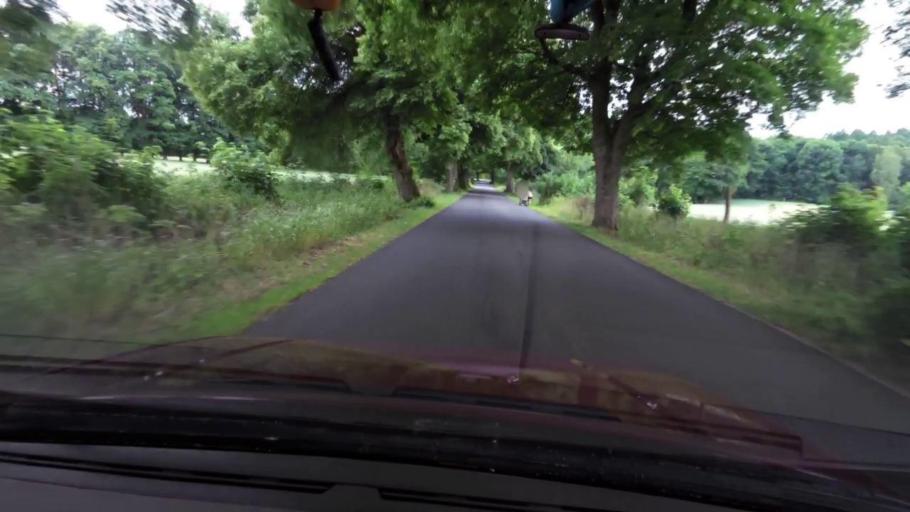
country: PL
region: Pomeranian Voivodeship
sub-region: Powiat slupski
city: Kepice
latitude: 54.2140
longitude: 16.8348
